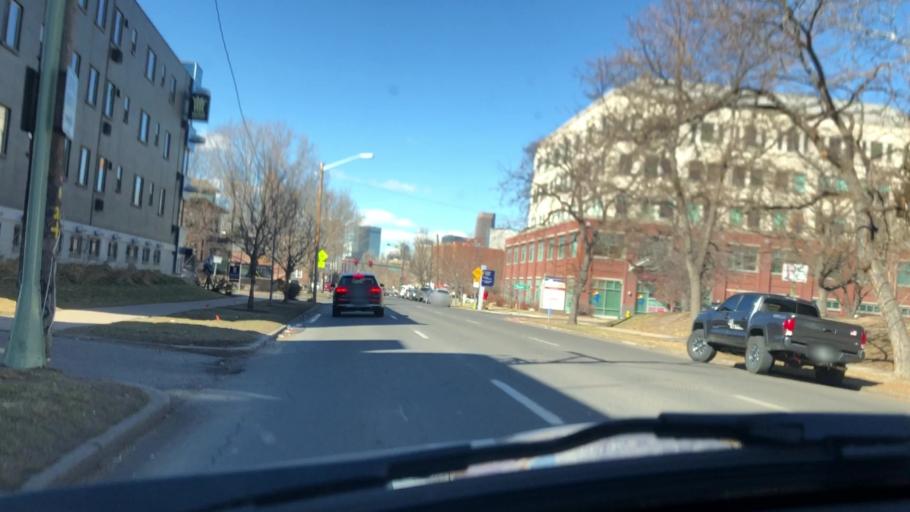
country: US
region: Colorado
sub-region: Denver County
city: Denver
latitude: 39.7448
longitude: -104.9665
